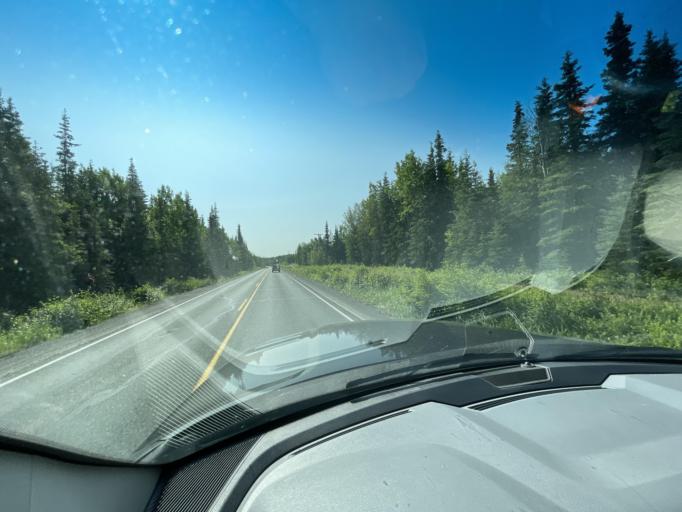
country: US
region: Alaska
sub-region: Kenai Peninsula Borough
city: Cohoe
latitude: 60.3042
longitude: -151.2862
